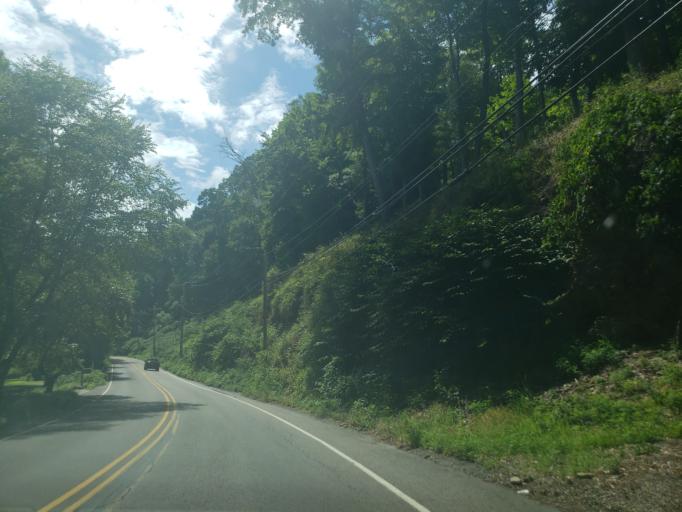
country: US
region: Pennsylvania
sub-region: Allegheny County
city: Coraopolis
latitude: 40.5382
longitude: -80.1582
